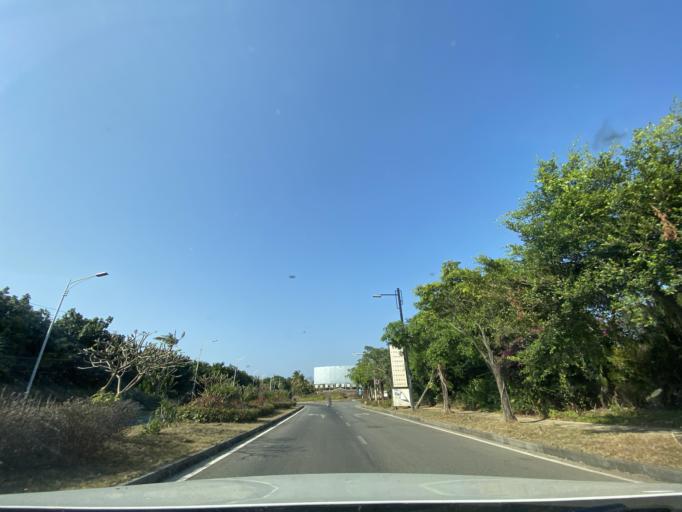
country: CN
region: Hainan
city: Yingzhou
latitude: 18.4459
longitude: 109.8461
